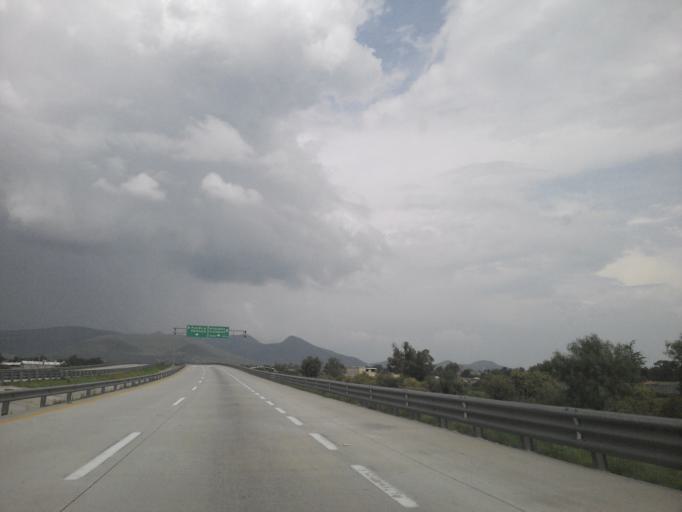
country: MX
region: Hidalgo
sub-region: Atitalaquia
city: Atitalaquia
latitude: 20.0682
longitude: -99.2245
